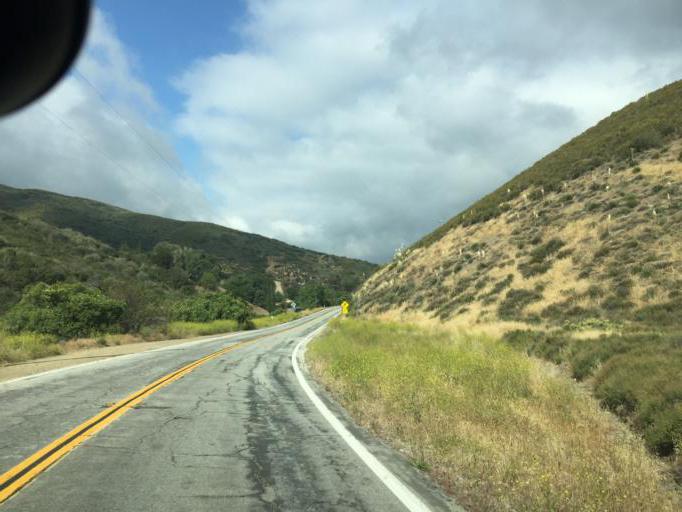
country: US
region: California
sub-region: Los Angeles County
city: Leona Valley
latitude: 34.5847
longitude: -118.3070
